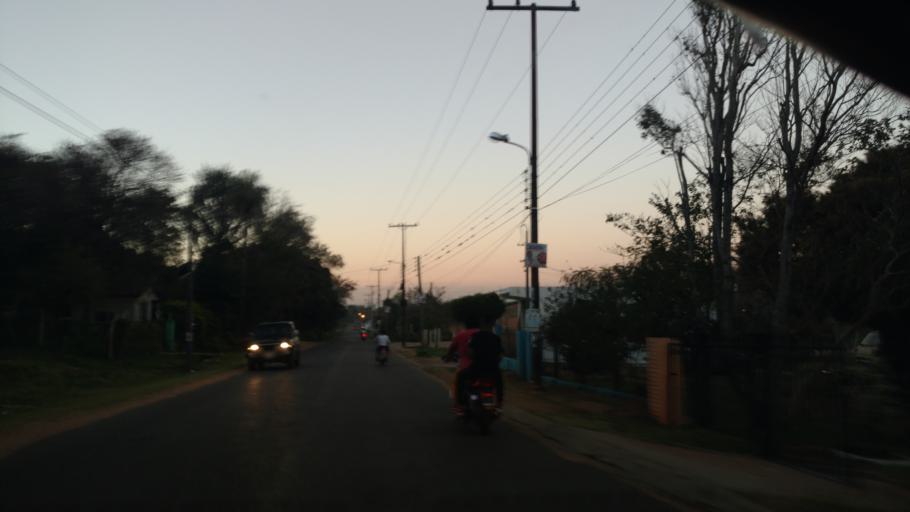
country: PY
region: Central
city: Guarambare
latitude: -25.4729
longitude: -57.4115
